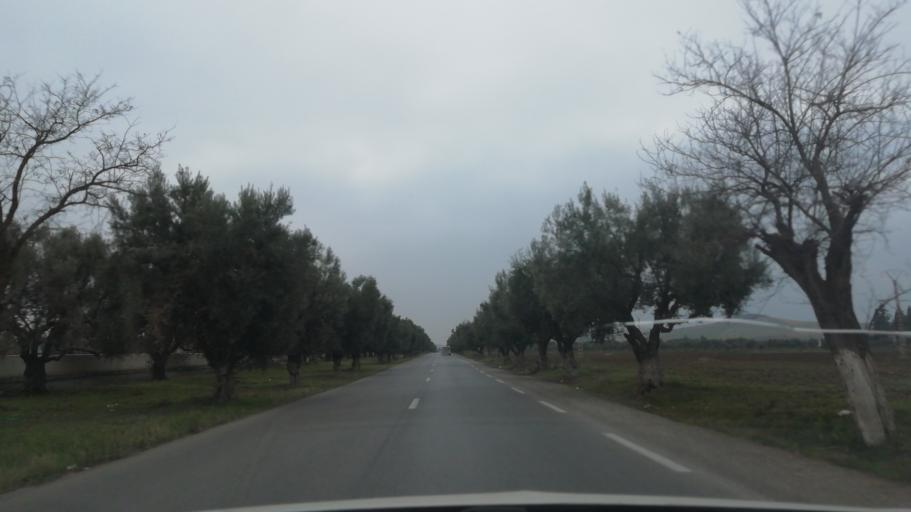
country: DZ
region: Sidi Bel Abbes
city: Sfizef
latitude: 35.2176
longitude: -0.3038
